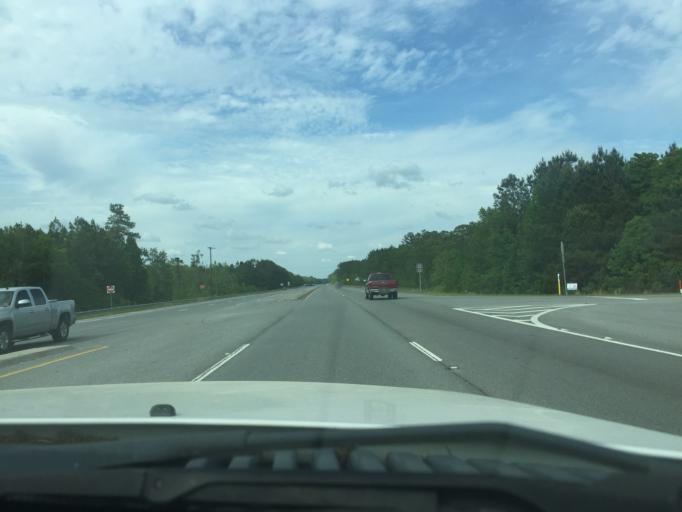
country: US
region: Georgia
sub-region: Bryan County
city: Richmond Hill
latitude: 31.9802
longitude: -81.2873
